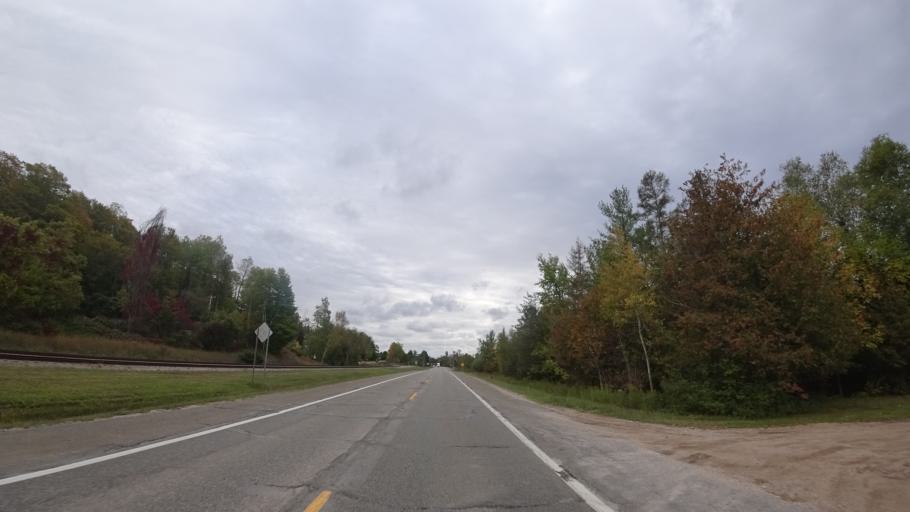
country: US
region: Michigan
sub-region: Charlevoix County
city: Boyne City
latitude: 45.1634
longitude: -84.9181
